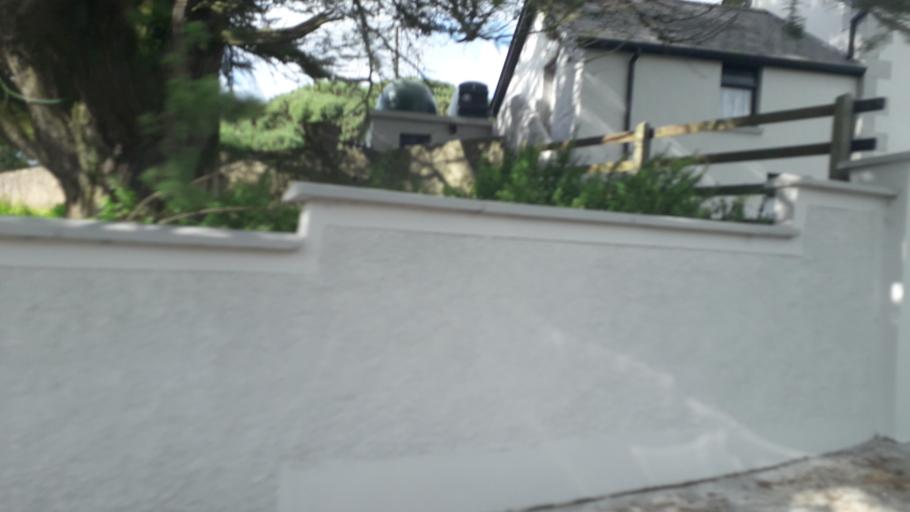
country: GB
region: Northern Ireland
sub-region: Down District
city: Warrenpoint
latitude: 54.0318
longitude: -6.2813
